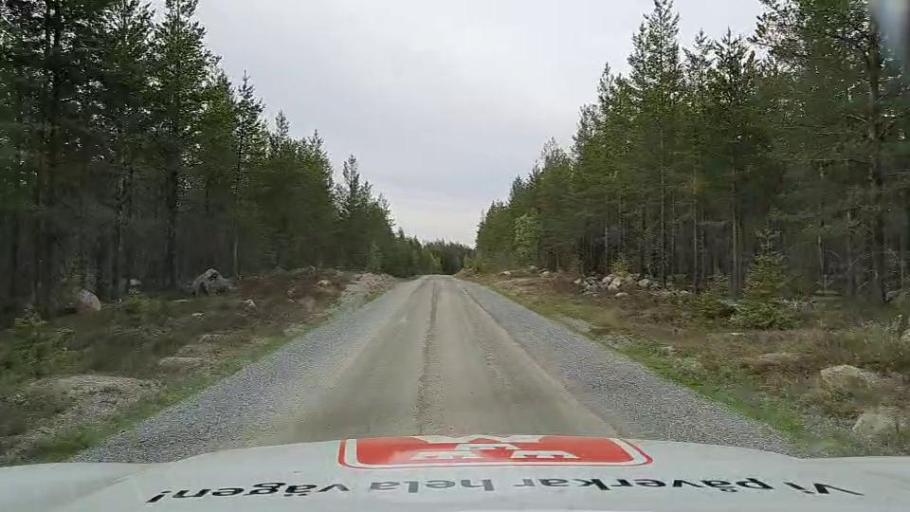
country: SE
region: Jaemtland
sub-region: Braecke Kommun
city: Braecke
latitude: 62.4682
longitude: 14.9172
